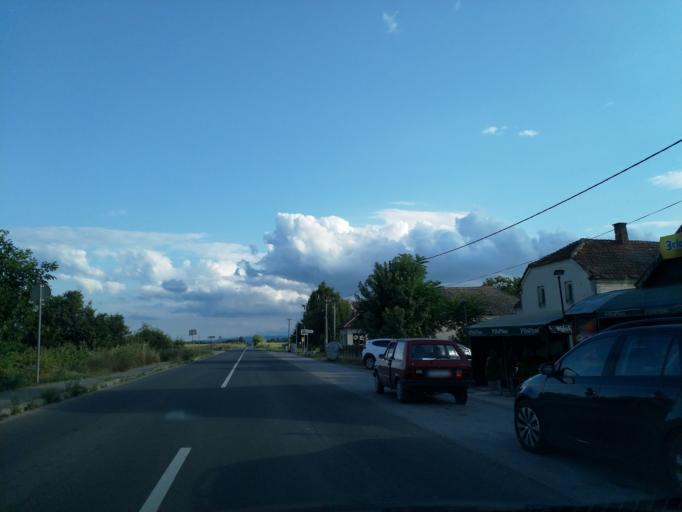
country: RS
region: Central Serbia
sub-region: Pomoravski Okrug
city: Paracin
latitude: 43.8019
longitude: 21.4219
